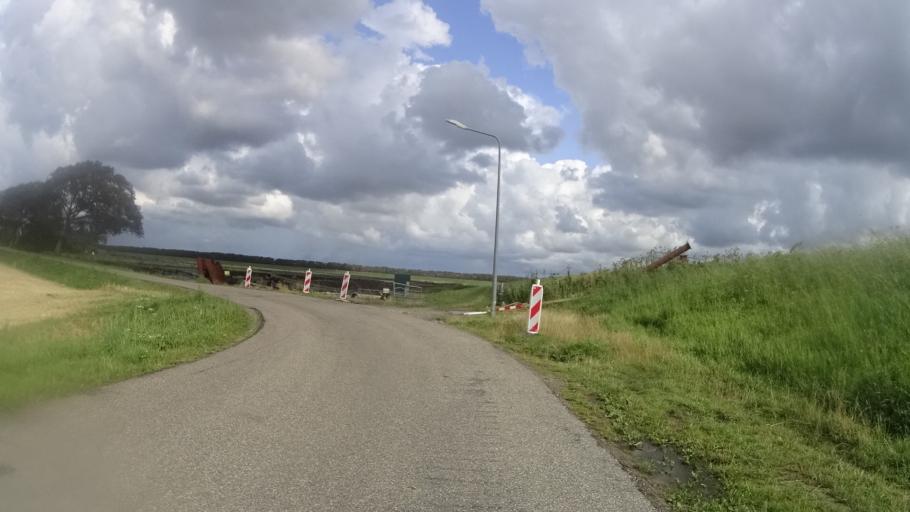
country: NL
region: North Holland
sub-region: Gemeente Schagen
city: Schagen
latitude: 52.8431
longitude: 4.8725
